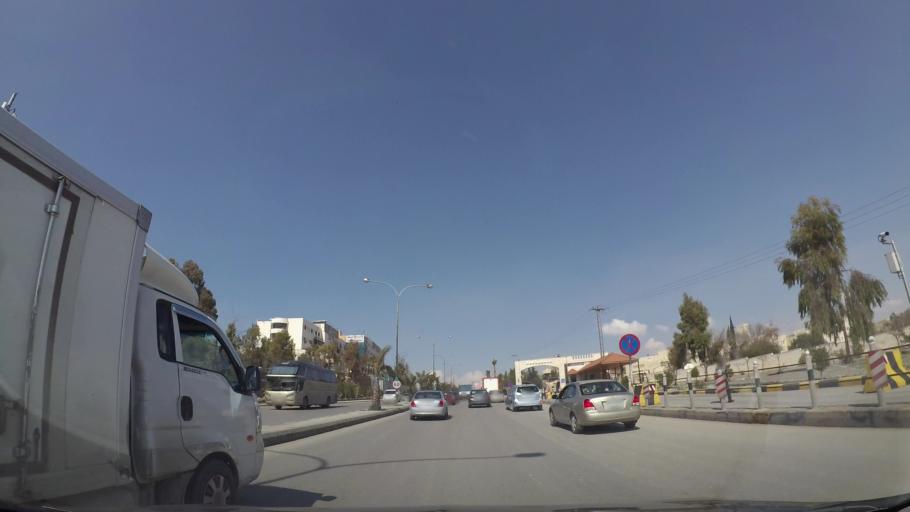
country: JO
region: Zarqa
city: Zarqa
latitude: 32.0522
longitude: 36.0936
